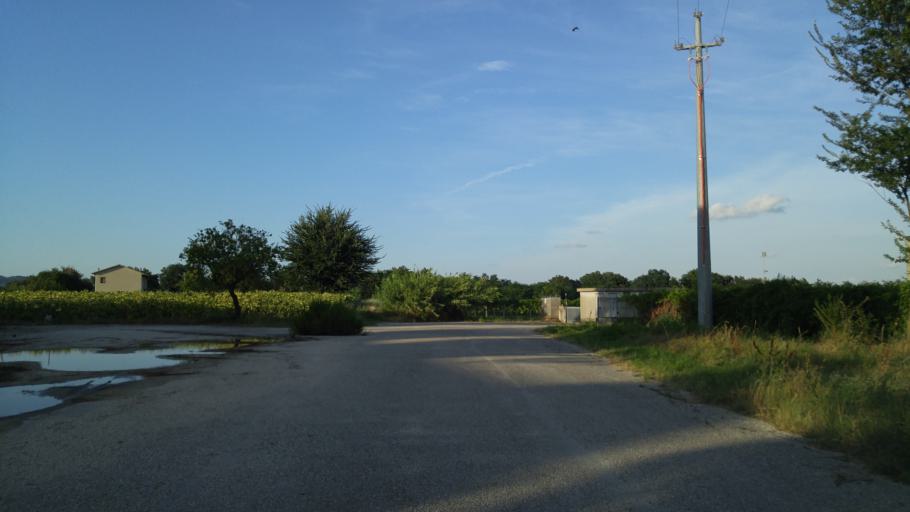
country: IT
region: The Marches
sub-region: Provincia di Pesaro e Urbino
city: Lucrezia
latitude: 43.7647
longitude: 12.9368
